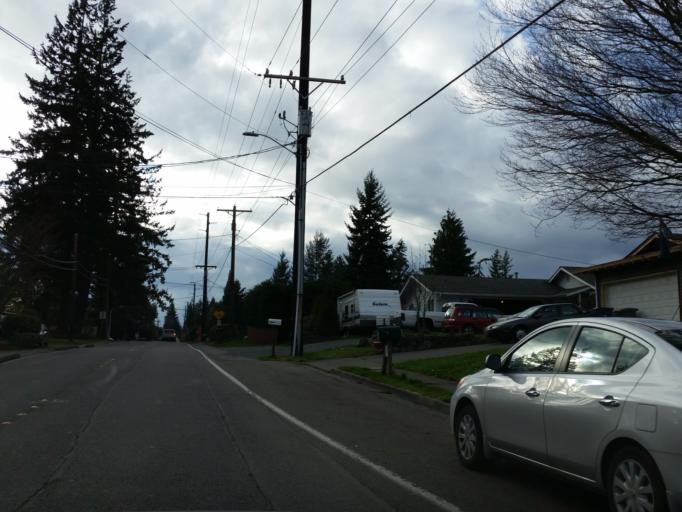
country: US
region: Washington
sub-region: Snohomish County
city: Lynnwood
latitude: 47.8285
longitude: -122.3178
